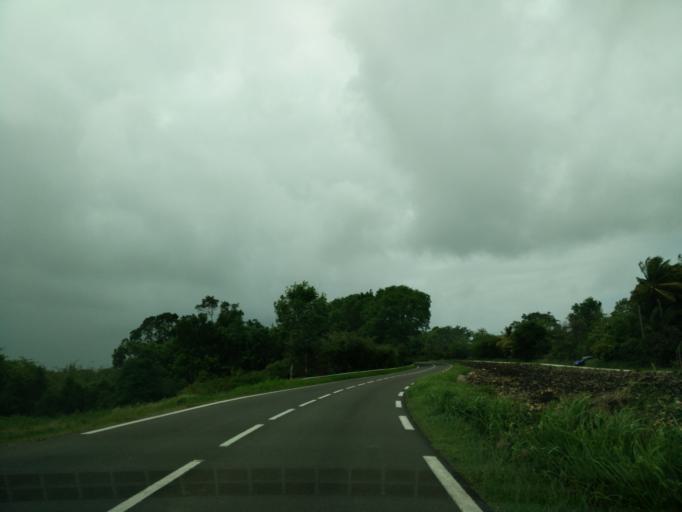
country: GP
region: Guadeloupe
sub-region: Guadeloupe
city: Grand-Bourg
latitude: 15.9062
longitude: -61.2592
